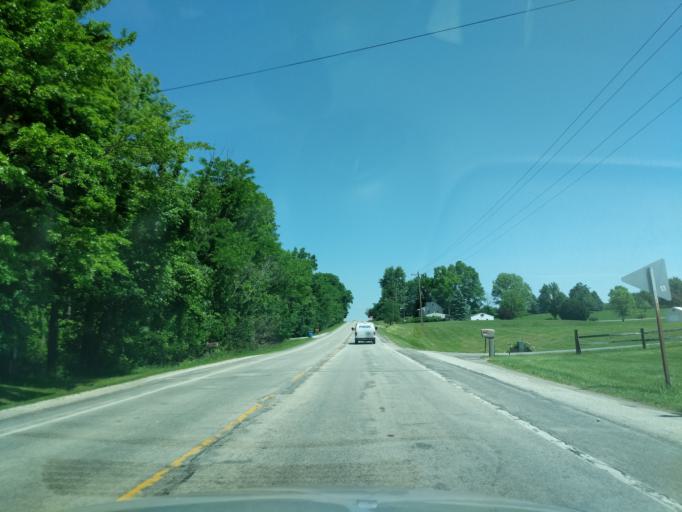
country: US
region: Indiana
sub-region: Whitley County
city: Columbia City
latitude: 41.1268
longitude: -85.4813
